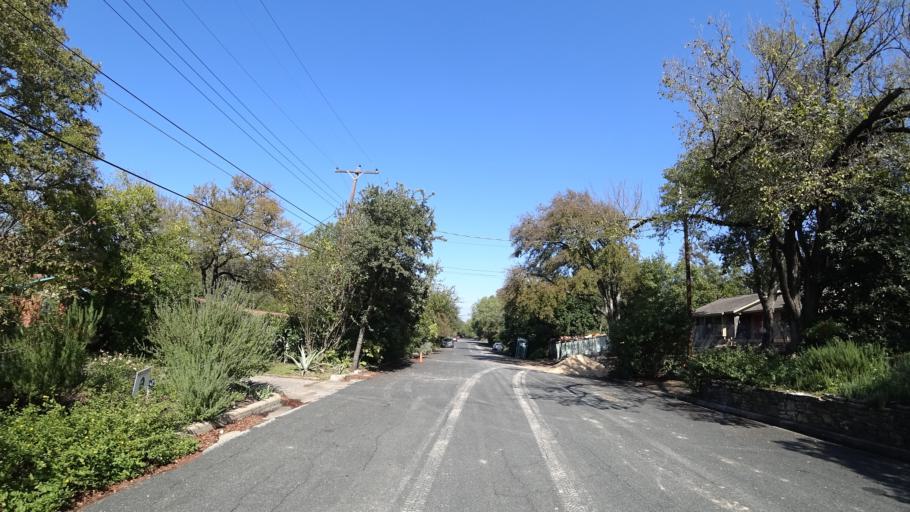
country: US
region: Texas
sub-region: Travis County
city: Rollingwood
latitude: 30.2582
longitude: -97.7704
